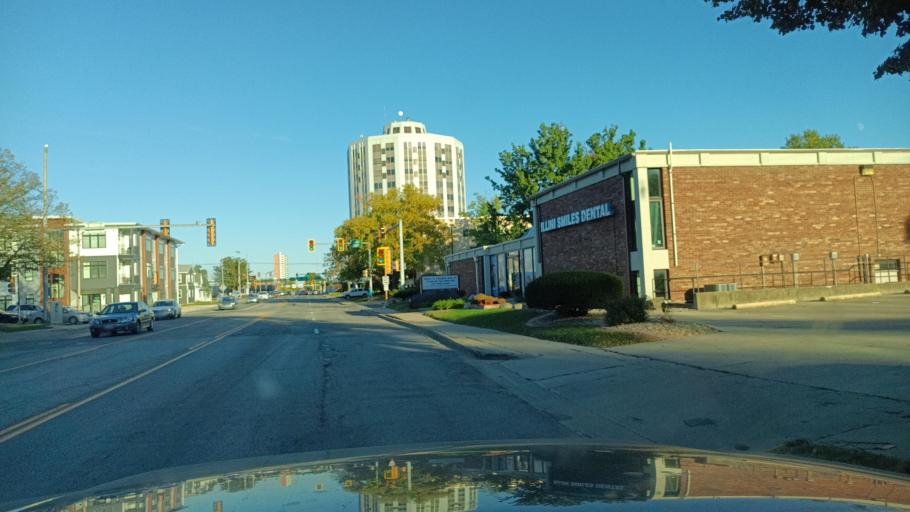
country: US
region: Illinois
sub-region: Champaign County
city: Champaign
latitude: 40.1126
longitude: -88.2476
